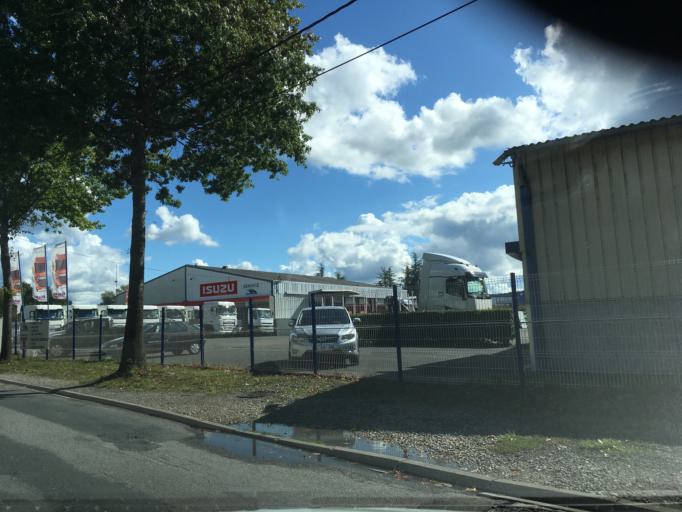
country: FR
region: Limousin
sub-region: Departement de la Correze
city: Saint-Pantaleon-de-Larche
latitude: 45.1569
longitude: 1.4744
